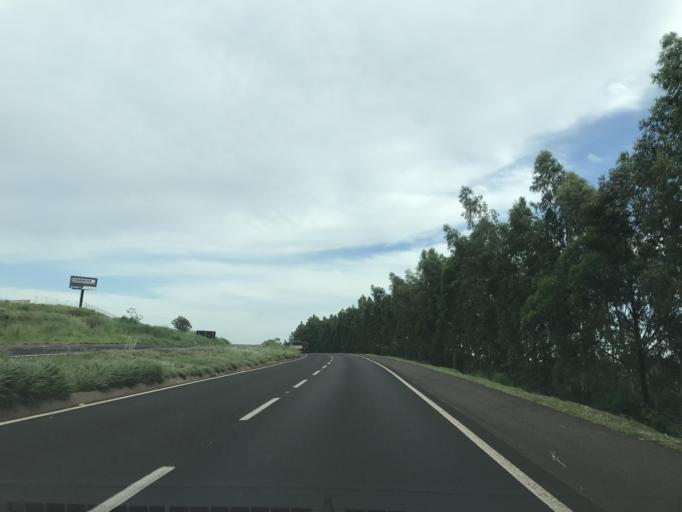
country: BR
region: Parana
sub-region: Alto Parana
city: Alto Parana
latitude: -23.1235
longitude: -52.3087
